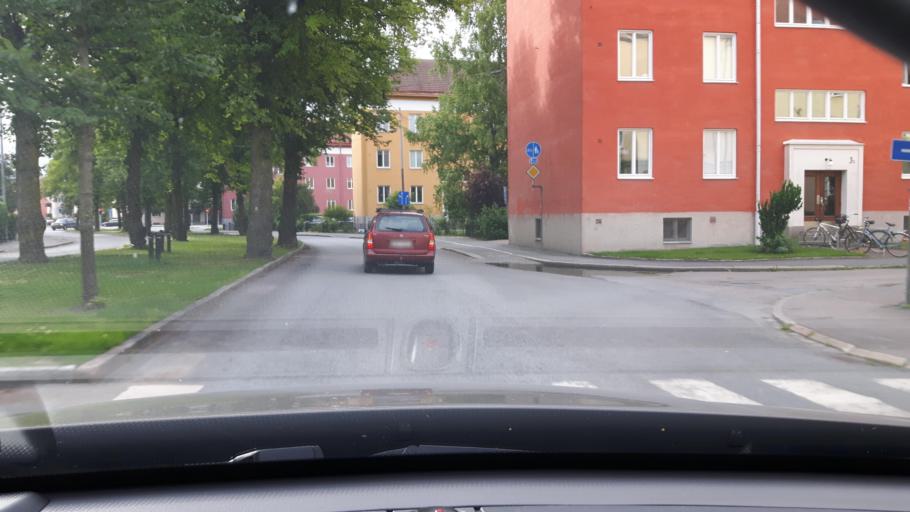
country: SE
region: Uppsala
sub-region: Uppsala Kommun
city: Uppsala
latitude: 59.8591
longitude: 17.6530
